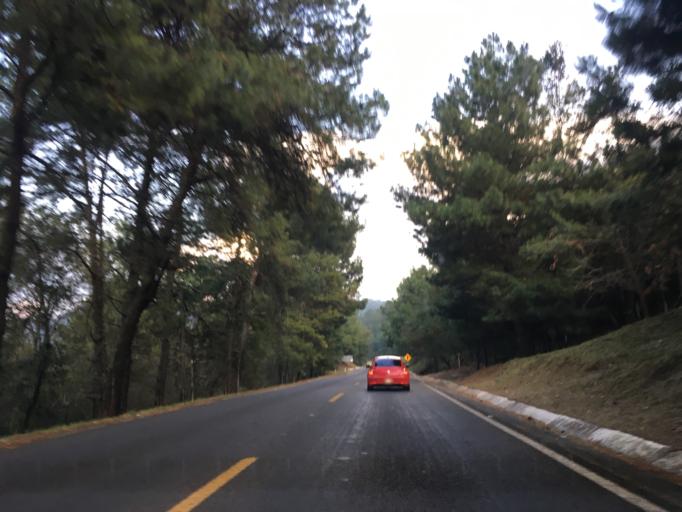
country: MX
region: Michoacan
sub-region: Patzcuaro
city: Santa Maria Huiramangaro (San Juan Tumbio)
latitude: 19.4825
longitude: -101.7361
